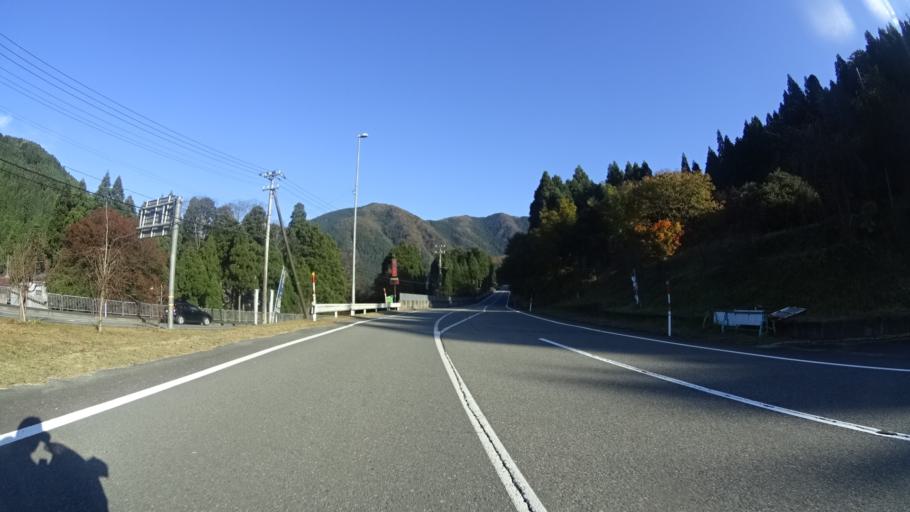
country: JP
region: Fukui
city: Maruoka
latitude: 36.1662
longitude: 136.3319
